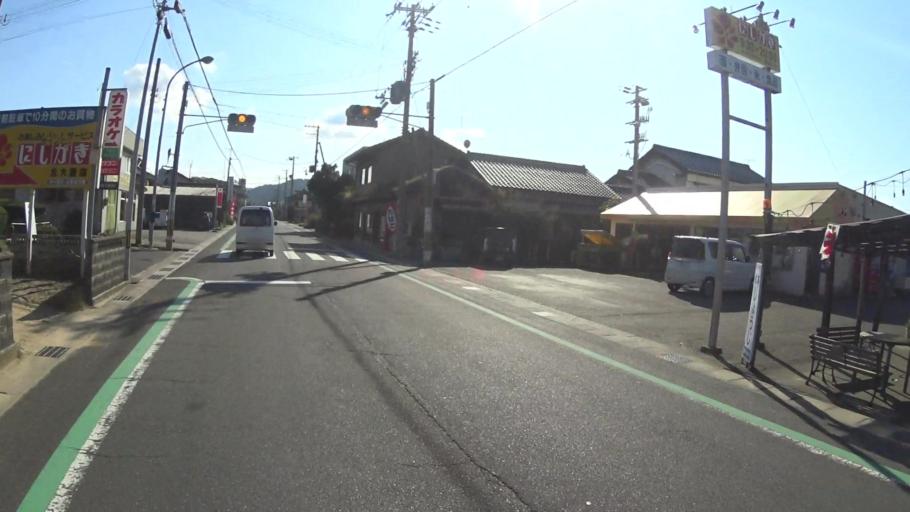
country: JP
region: Kyoto
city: Miyazu
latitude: 35.6861
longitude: 135.0326
